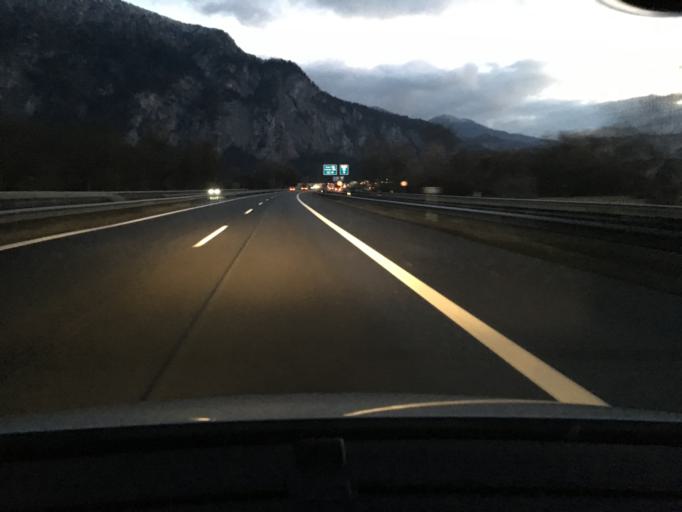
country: DE
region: Bavaria
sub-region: Upper Bavaria
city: Kiefersfelden
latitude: 47.6188
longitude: 12.2022
